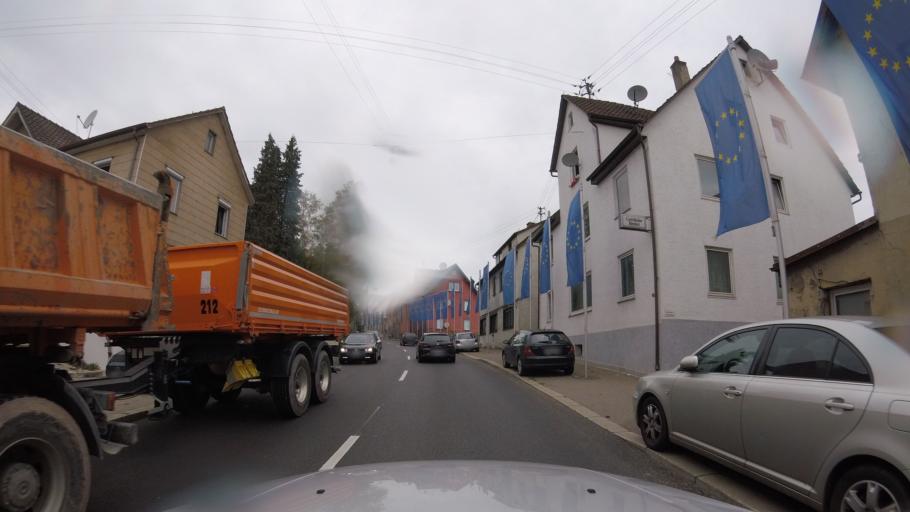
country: DE
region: Baden-Wuerttemberg
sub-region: Regierungsbezirk Stuttgart
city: Schwabisch Gmund
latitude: 48.8058
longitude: 9.8004
